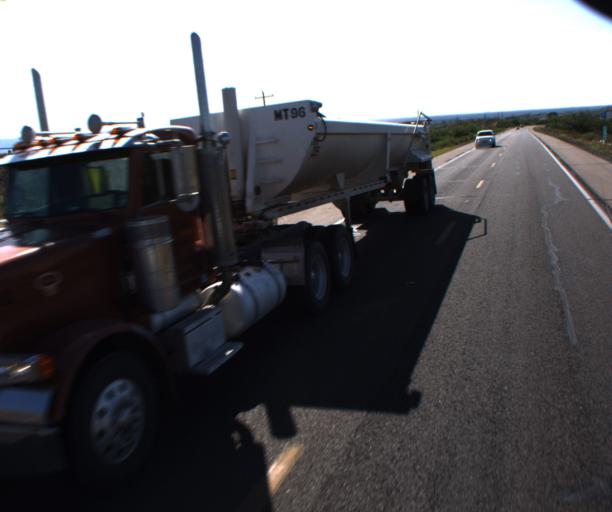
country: US
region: Arizona
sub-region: Cochise County
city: Benson
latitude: 31.9216
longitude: -110.2692
